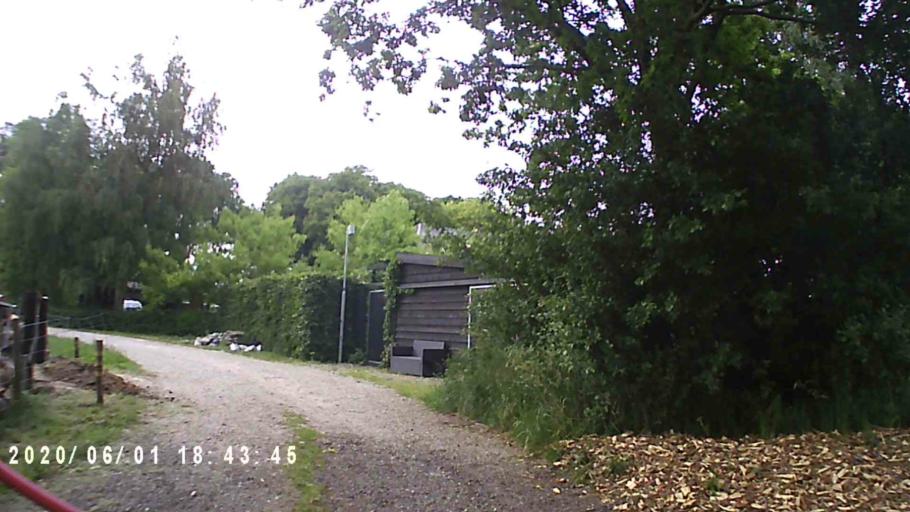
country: NL
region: Friesland
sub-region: Gemeente Tytsjerksteradiel
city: Eastermar
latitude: 53.1755
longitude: 6.0655
